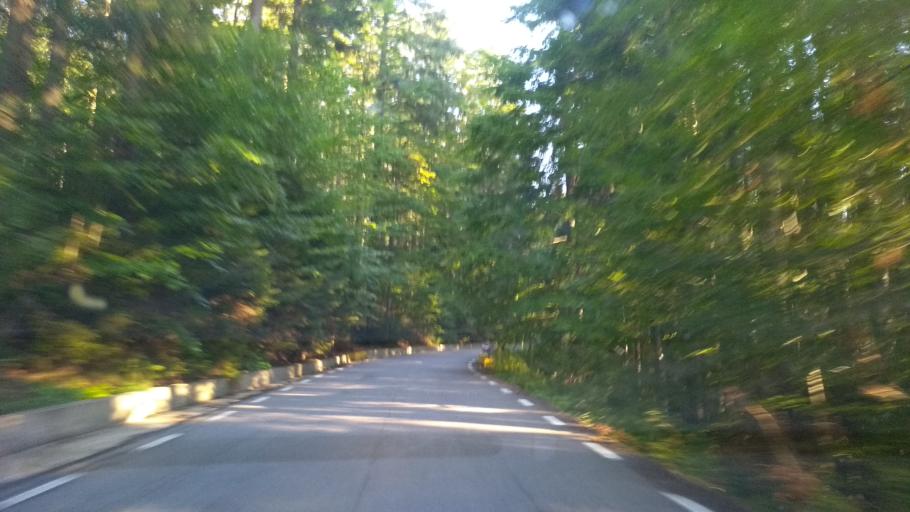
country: RO
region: Prahova
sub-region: Oras Sinaia
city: Sinaia
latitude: 45.3145
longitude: 25.5201
